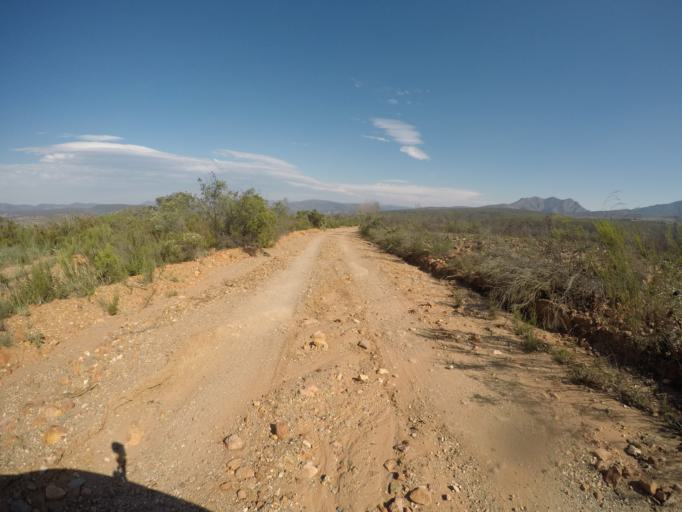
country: ZA
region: Eastern Cape
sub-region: Cacadu District Municipality
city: Kareedouw
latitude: -33.6365
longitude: 24.4535
